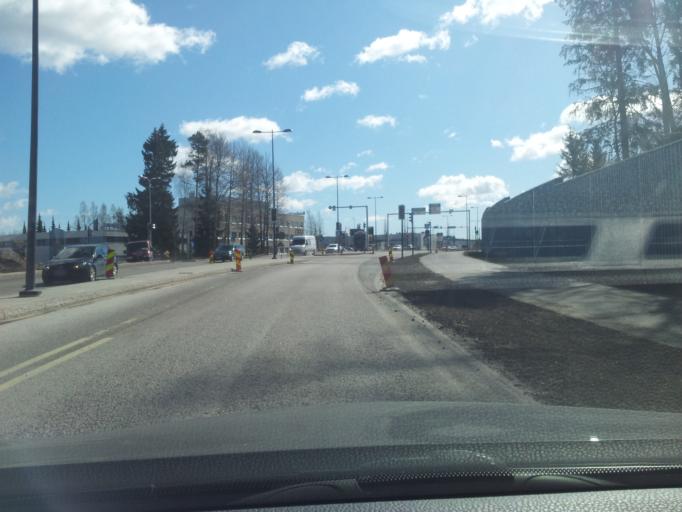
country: FI
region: Uusimaa
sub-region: Helsinki
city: Kauniainen
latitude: 60.1660
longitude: 24.7007
